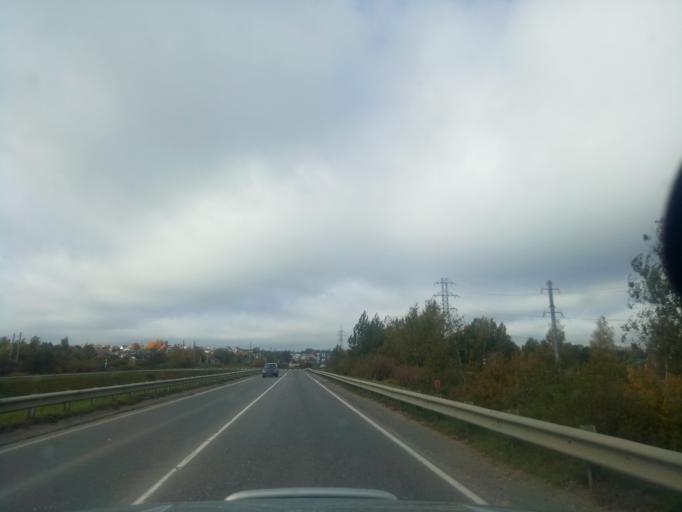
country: BY
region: Minsk
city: Zaslawye
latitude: 54.0002
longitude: 27.2795
